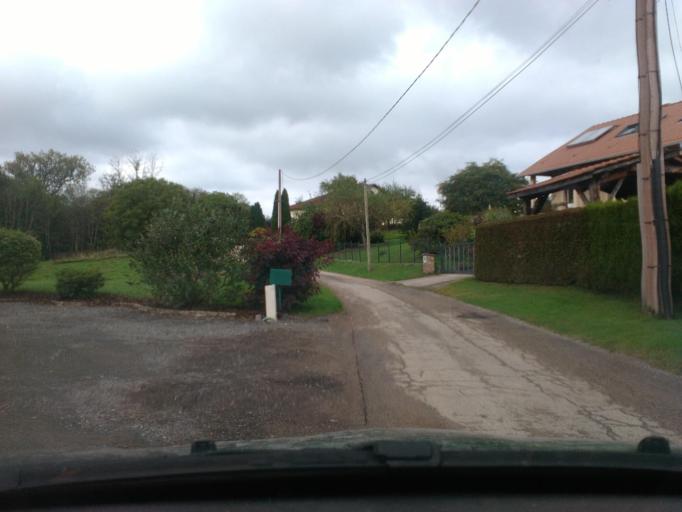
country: FR
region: Lorraine
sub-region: Departement des Vosges
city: Saint-Michel-sur-Meurthe
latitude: 48.3341
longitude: 6.8655
